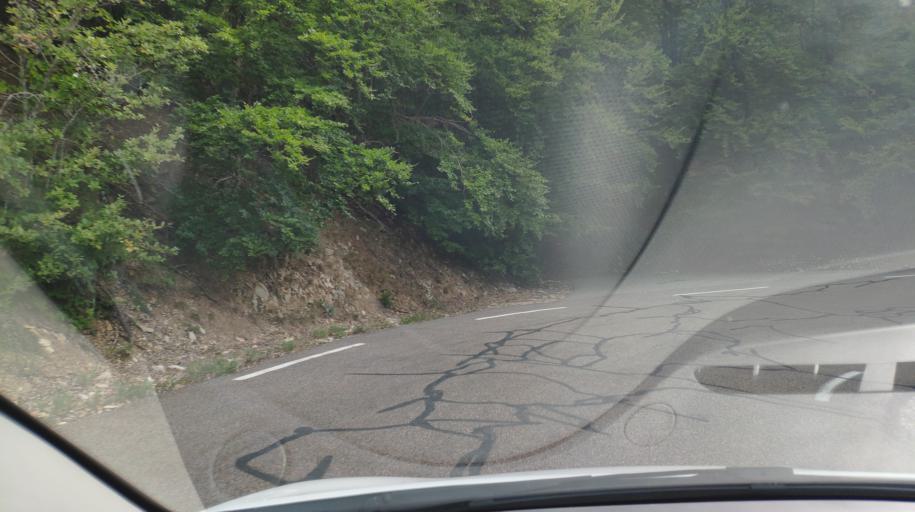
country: FR
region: Provence-Alpes-Cote d'Azur
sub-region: Departement du Vaucluse
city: Sault
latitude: 44.1572
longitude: 5.3493
